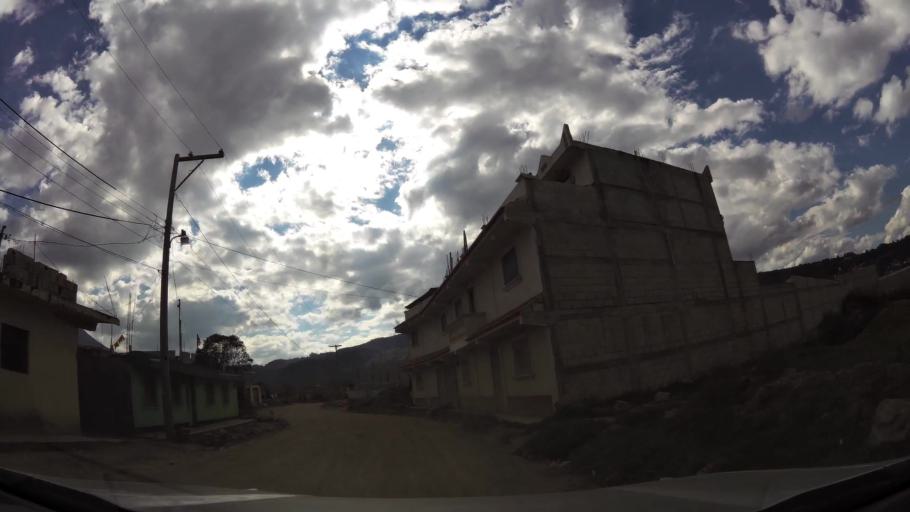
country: GT
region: Quetzaltenango
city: Quetzaltenango
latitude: 14.8273
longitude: -91.5404
